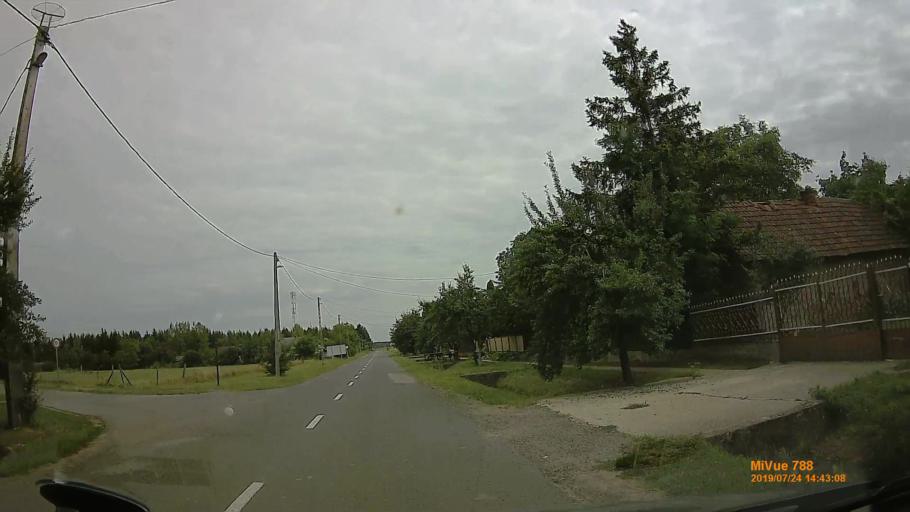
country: HU
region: Szabolcs-Szatmar-Bereg
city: Mandok
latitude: 48.3128
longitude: 22.2752
